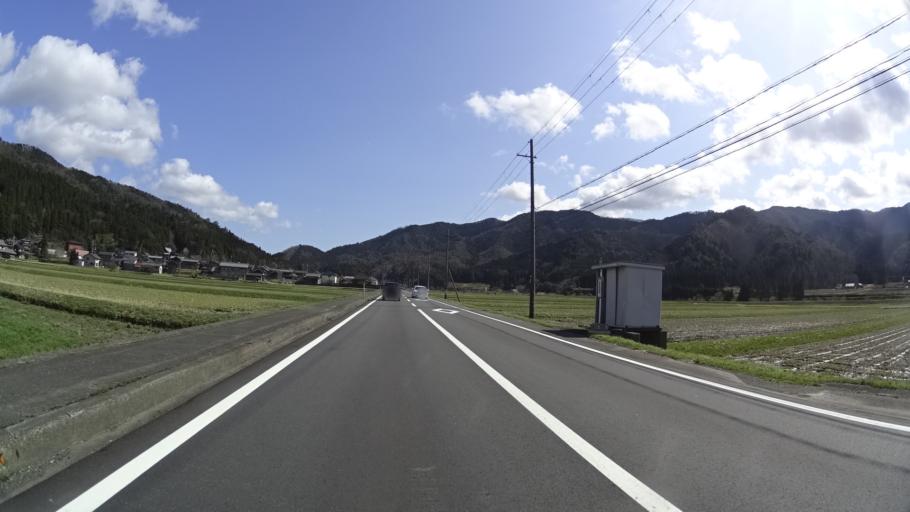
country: JP
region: Fukui
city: Obama
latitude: 35.4562
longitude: 135.8789
